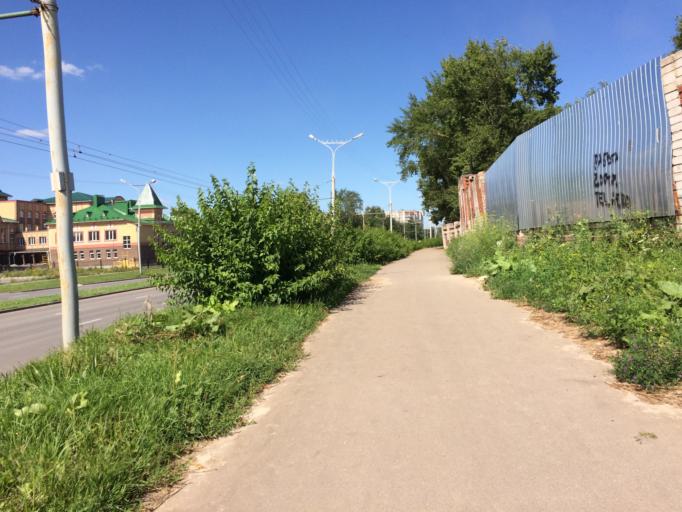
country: RU
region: Mariy-El
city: Yoshkar-Ola
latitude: 56.6277
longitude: 47.9364
